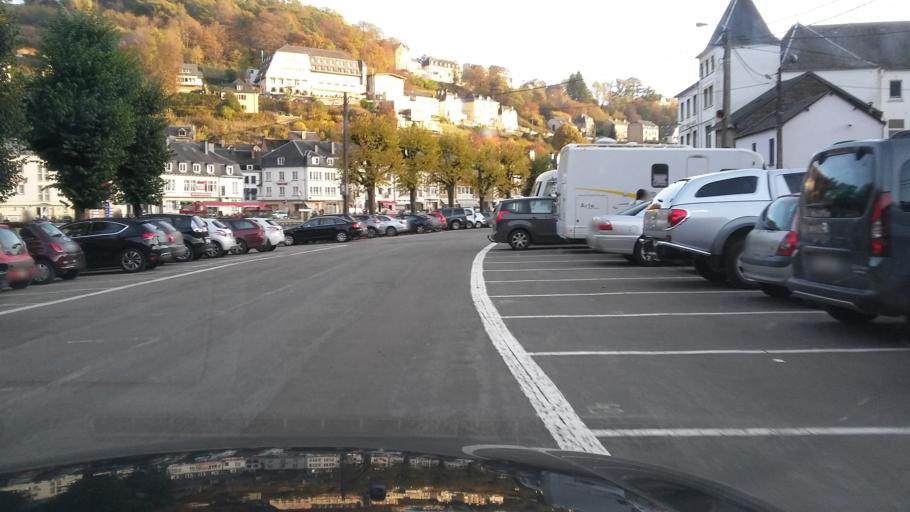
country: BE
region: Wallonia
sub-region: Province du Luxembourg
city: Bouillon
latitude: 49.7968
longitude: 5.0698
